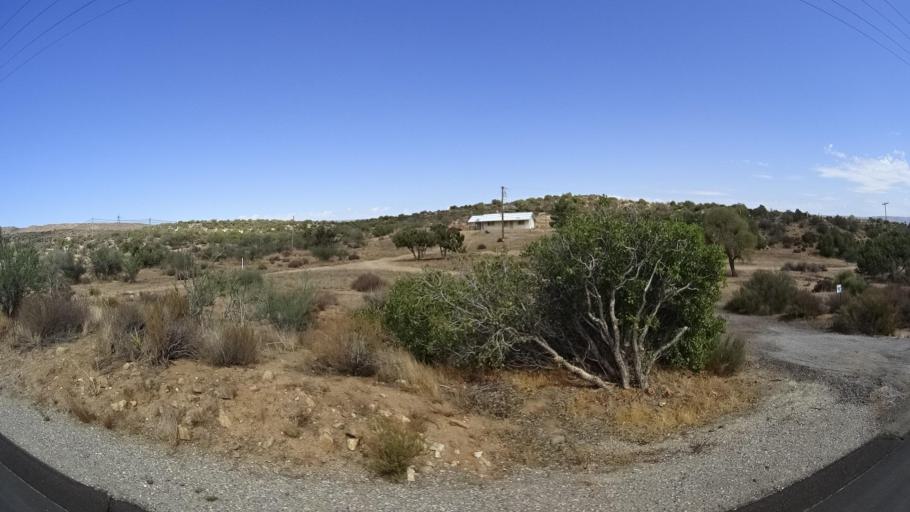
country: MX
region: Baja California
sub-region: Tecate
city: Cereso del Hongo
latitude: 32.6287
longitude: -116.2231
